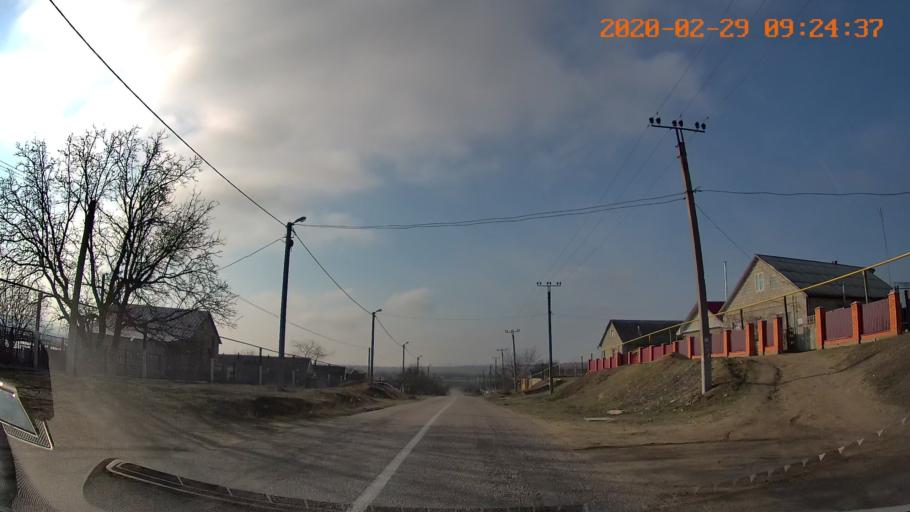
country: MD
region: Telenesti
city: Pervomaisc
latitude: 46.7144
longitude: 29.9581
